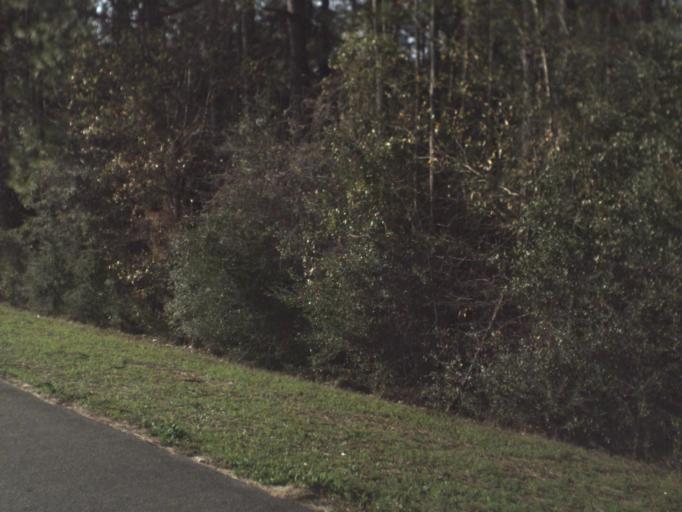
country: US
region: Florida
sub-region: Bay County
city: Laguna Beach
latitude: 30.4399
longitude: -85.8094
